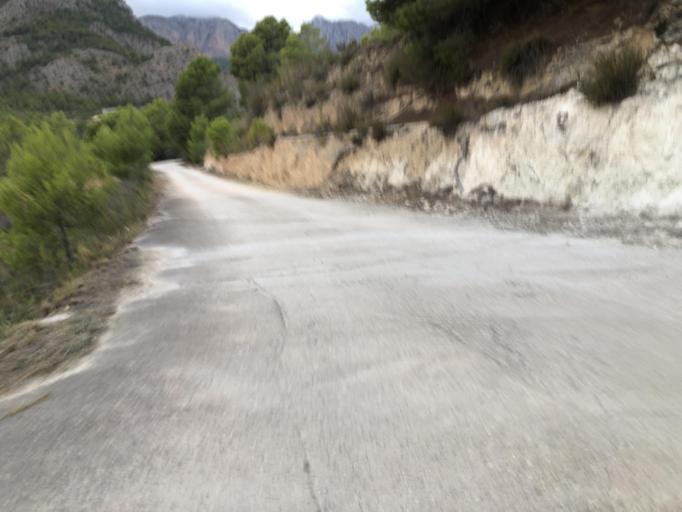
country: ES
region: Valencia
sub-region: Provincia de Alicante
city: Polop
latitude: 38.6354
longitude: -0.1453
